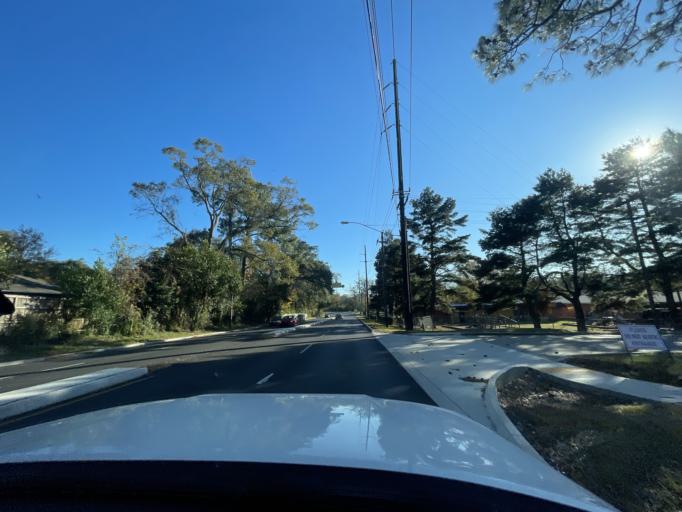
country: US
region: Louisiana
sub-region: East Baton Rouge Parish
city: Baton Rouge
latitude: 30.4307
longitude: -91.1528
